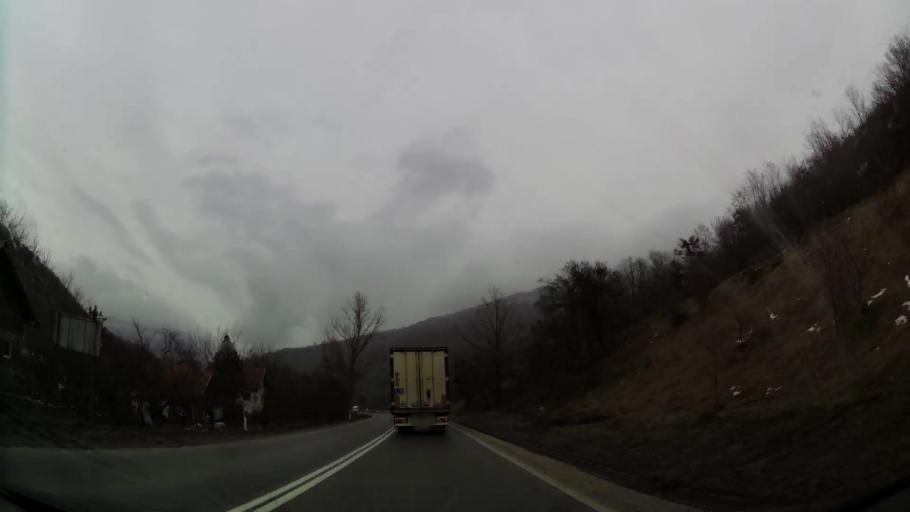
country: RS
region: Central Serbia
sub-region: Pcinjski Okrug
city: Vladicin Han
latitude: 42.7743
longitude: 22.0916
